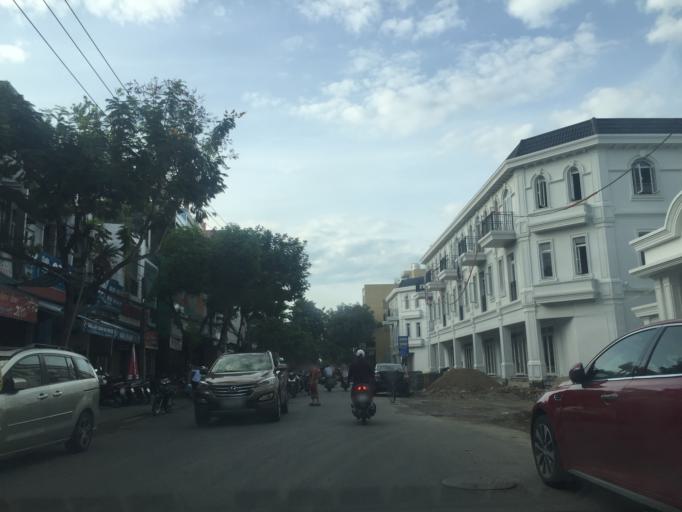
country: VN
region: Da Nang
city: Da Nang
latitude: 16.0749
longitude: 108.2125
